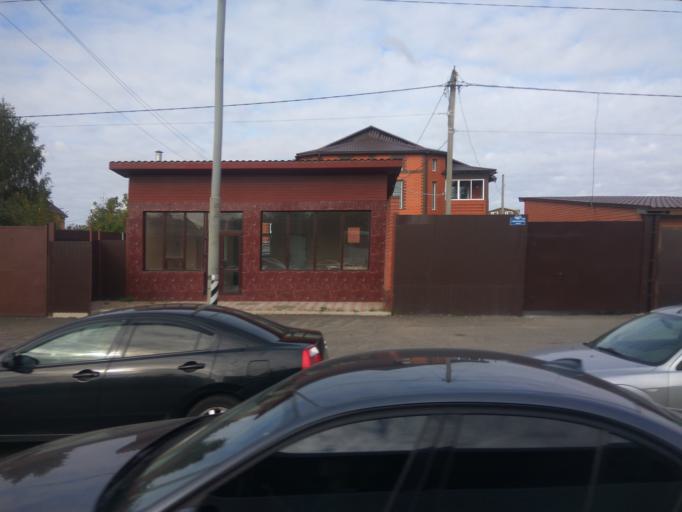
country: RU
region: Moskovskaya
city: Balashikha
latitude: 55.8386
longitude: 37.9473
